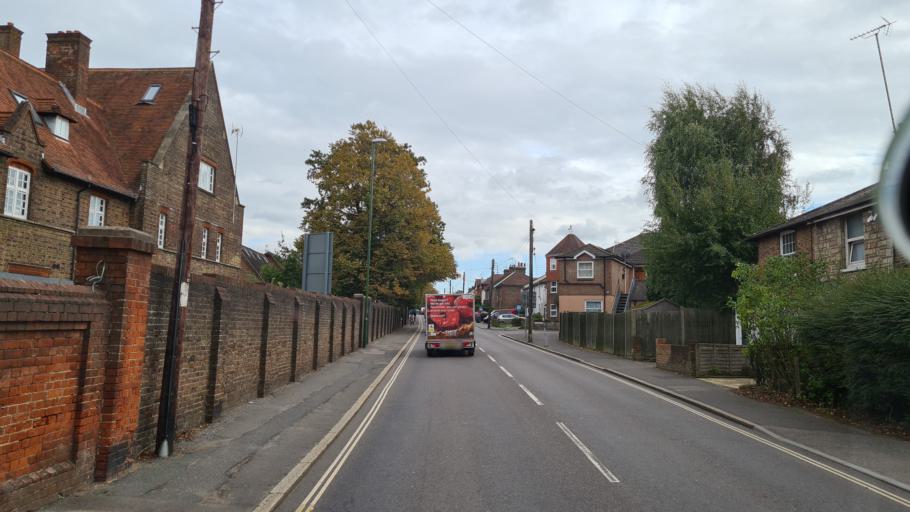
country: GB
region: England
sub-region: West Sussex
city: Haywards Heath
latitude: 50.9949
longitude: -0.0991
